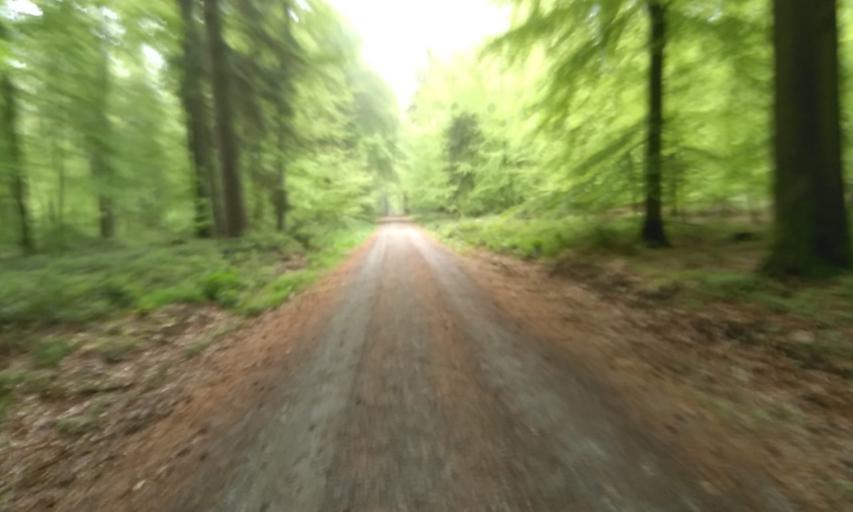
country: DE
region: Lower Saxony
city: Nottensdorf
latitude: 53.4717
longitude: 9.6375
